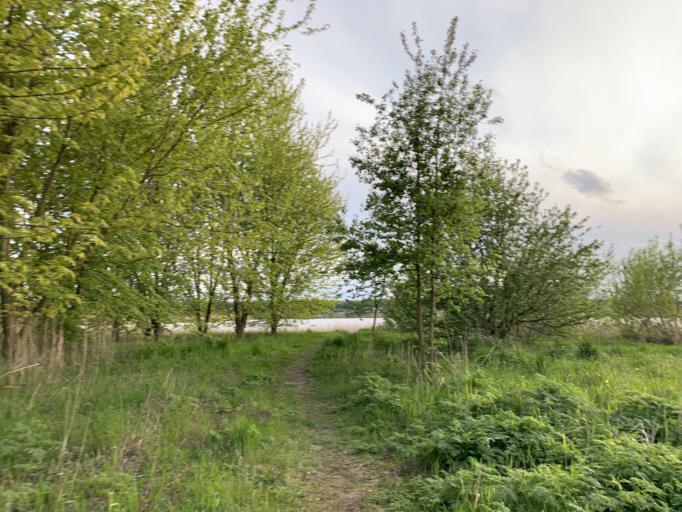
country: BY
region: Minsk
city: Nyasvizh
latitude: 53.2081
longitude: 26.6725
